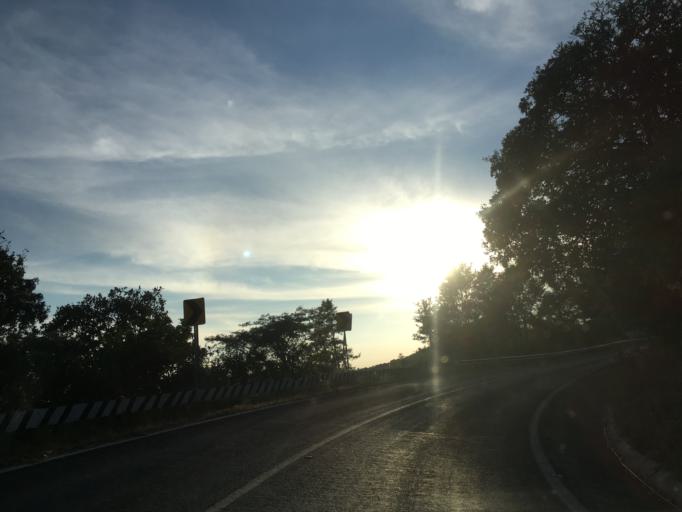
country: MX
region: Michoacan
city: Tzitzio
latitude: 19.6533
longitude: -100.9310
